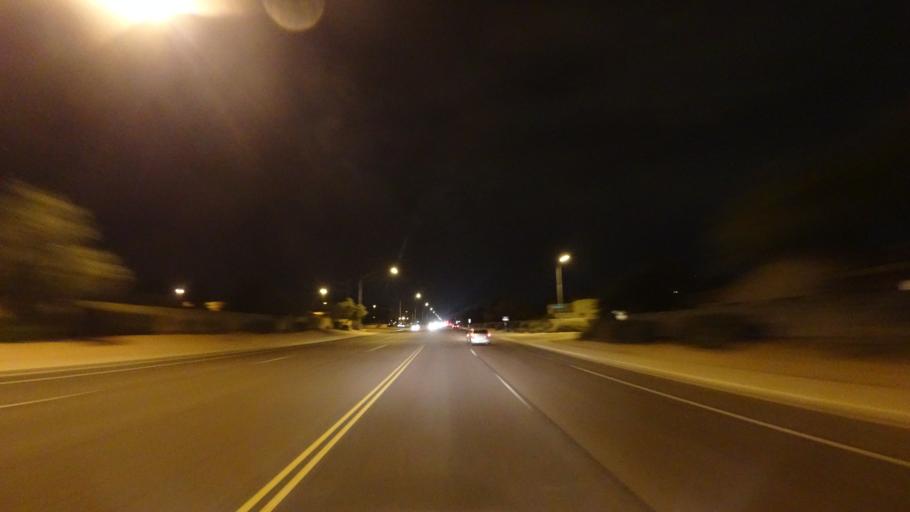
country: US
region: Arizona
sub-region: Maricopa County
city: Mesa
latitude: 33.4588
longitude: -111.7708
